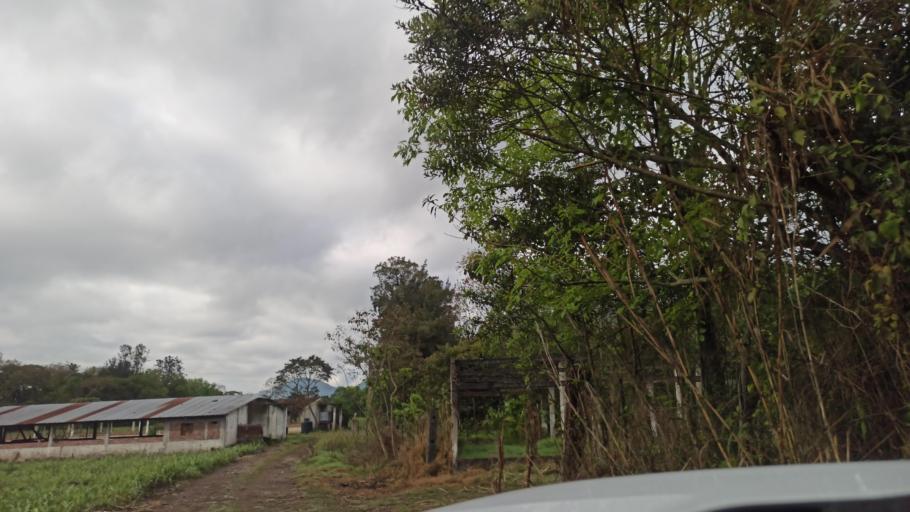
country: MX
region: Veracruz
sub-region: Chocaman
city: San Jose Neria
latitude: 19.0025
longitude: -97.0090
